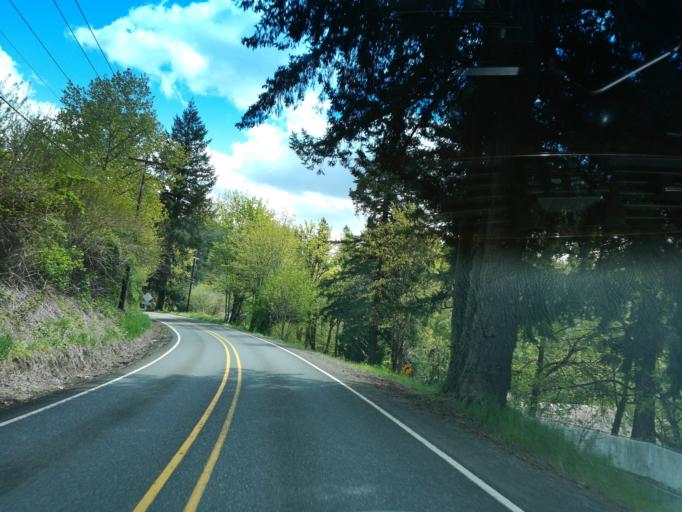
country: US
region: Oregon
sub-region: Clackamas County
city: Damascus
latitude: 45.4390
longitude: -122.4510
